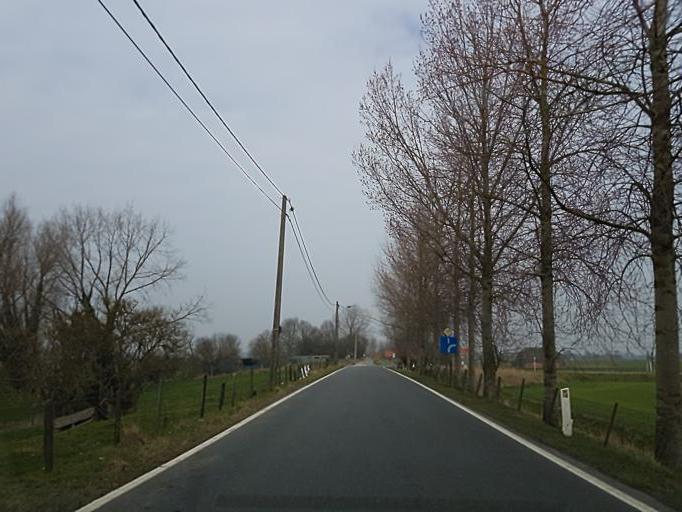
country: BE
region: Flanders
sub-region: Provincie Oost-Vlaanderen
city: Beveren
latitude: 51.3031
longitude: 4.2341
